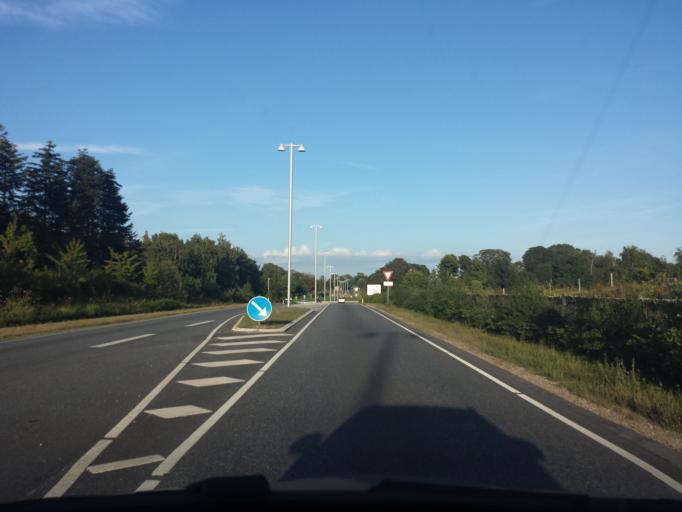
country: DK
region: Capital Region
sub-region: Frederikssund Kommune
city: Frederikssund
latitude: 55.8448
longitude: 12.0901
